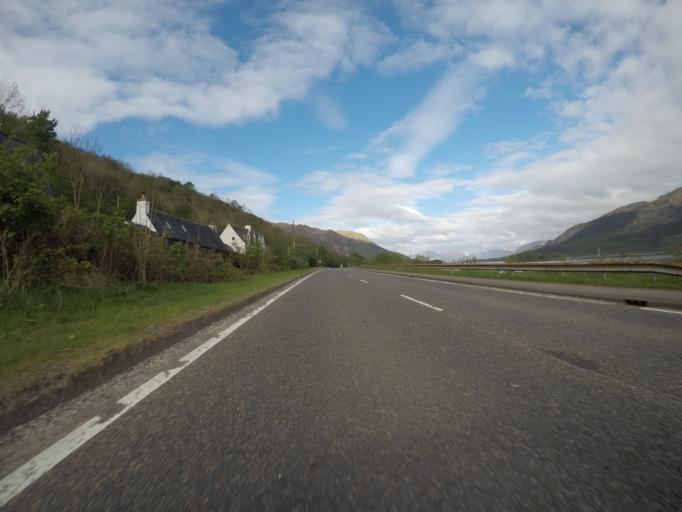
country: GB
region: Scotland
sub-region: Highland
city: Fort William
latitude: 56.6803
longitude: -5.1152
